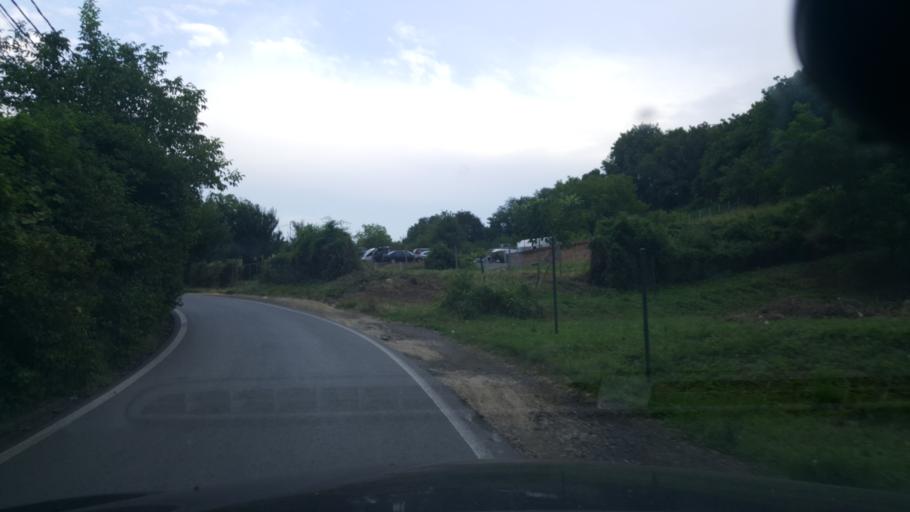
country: RS
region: Central Serbia
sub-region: Belgrade
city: Zvezdara
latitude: 44.7795
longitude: 20.5351
